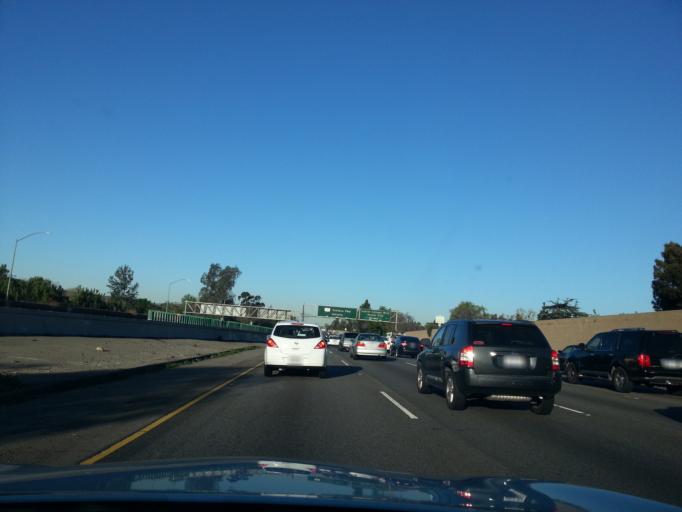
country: US
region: California
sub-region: Los Angeles County
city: North Hollywood
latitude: 34.1545
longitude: -118.3796
